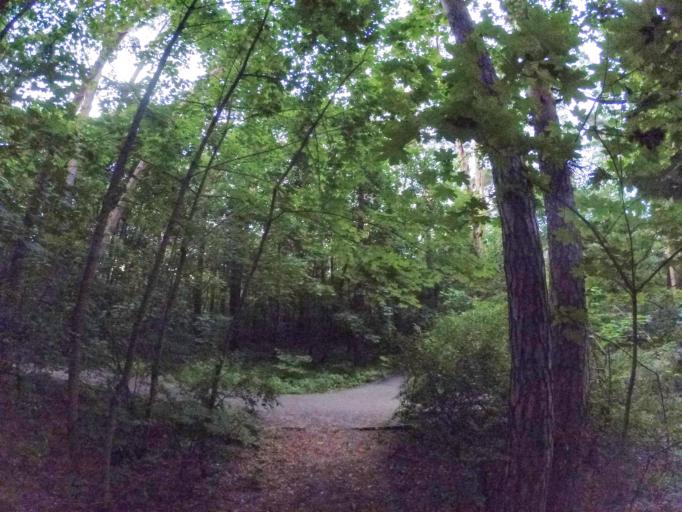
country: RU
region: Moscow
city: Shchukino
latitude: 55.7803
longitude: 37.4298
